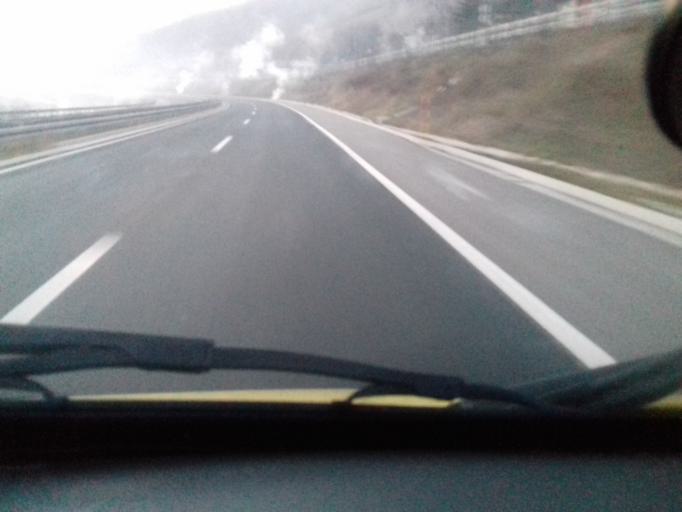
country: BA
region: Federation of Bosnia and Herzegovina
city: Kakanj
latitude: 44.1352
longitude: 18.0506
